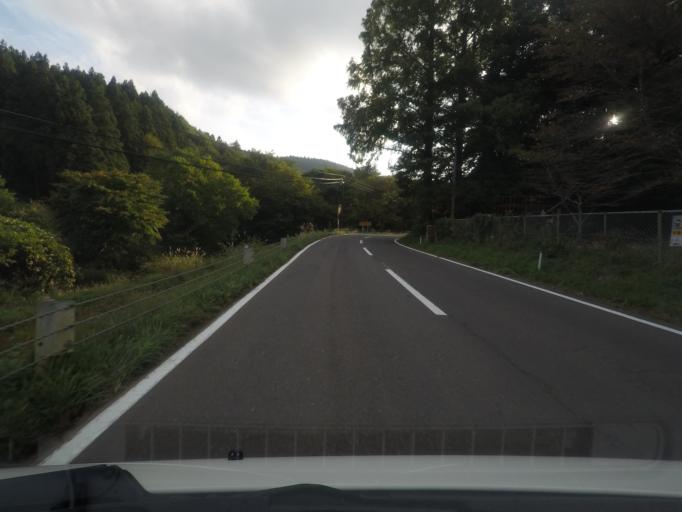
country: JP
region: Fukushima
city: Funehikimachi-funehiki
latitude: 37.5837
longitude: 140.6981
